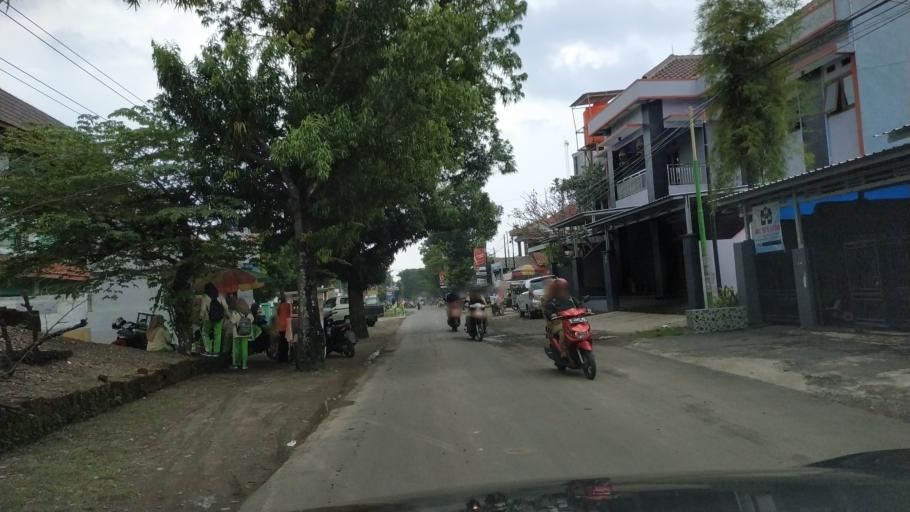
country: ID
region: Central Java
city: Slawi
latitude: -6.9923
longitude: 109.1207
